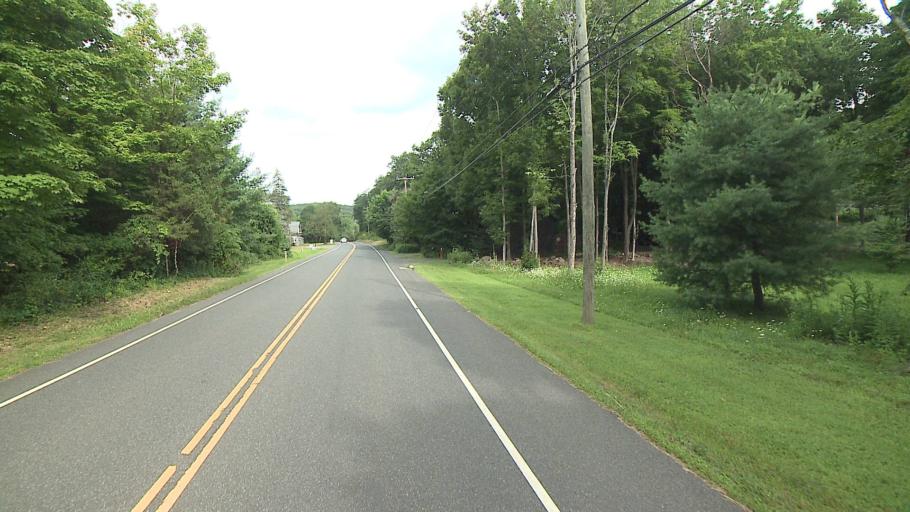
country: US
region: Connecticut
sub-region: Litchfield County
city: Woodbury
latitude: 41.5810
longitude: -73.2456
